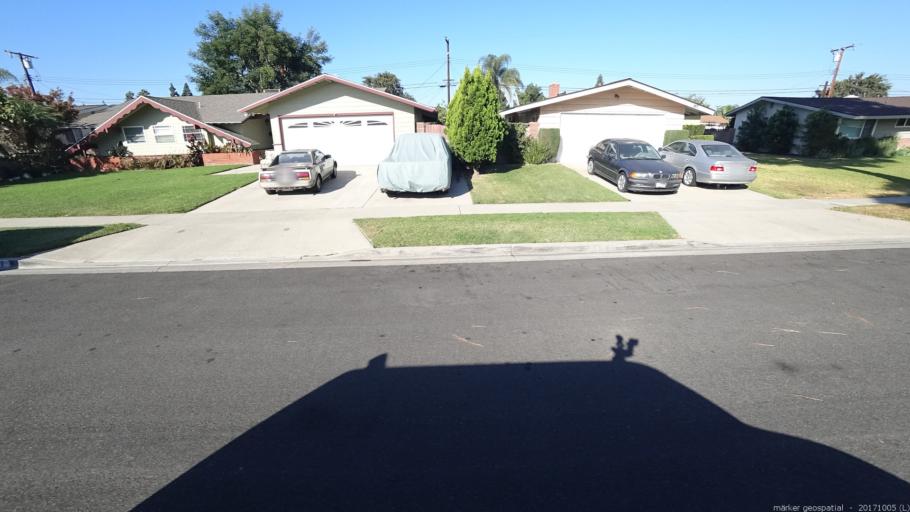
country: US
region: California
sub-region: Orange County
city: Garden Grove
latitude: 33.7990
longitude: -117.9479
